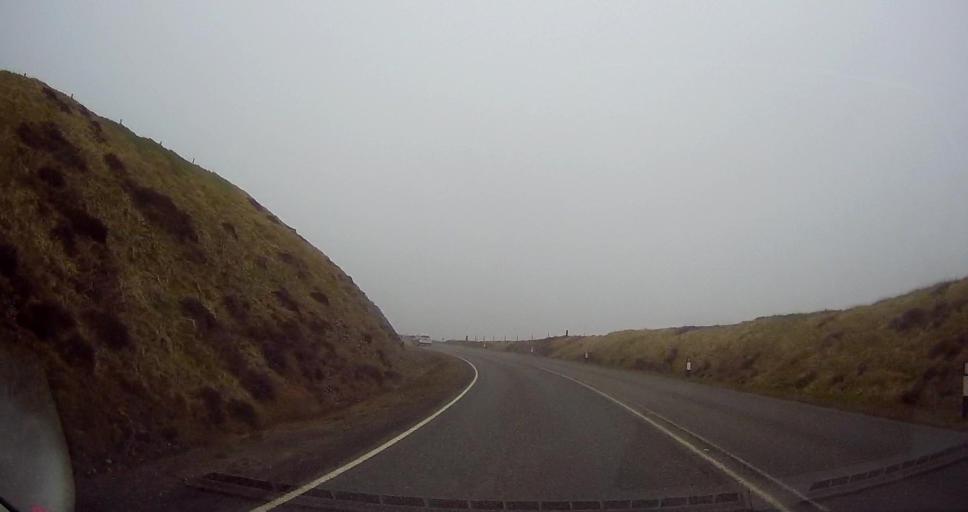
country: GB
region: Scotland
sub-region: Shetland Islands
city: Lerwick
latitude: 60.1371
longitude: -1.2302
